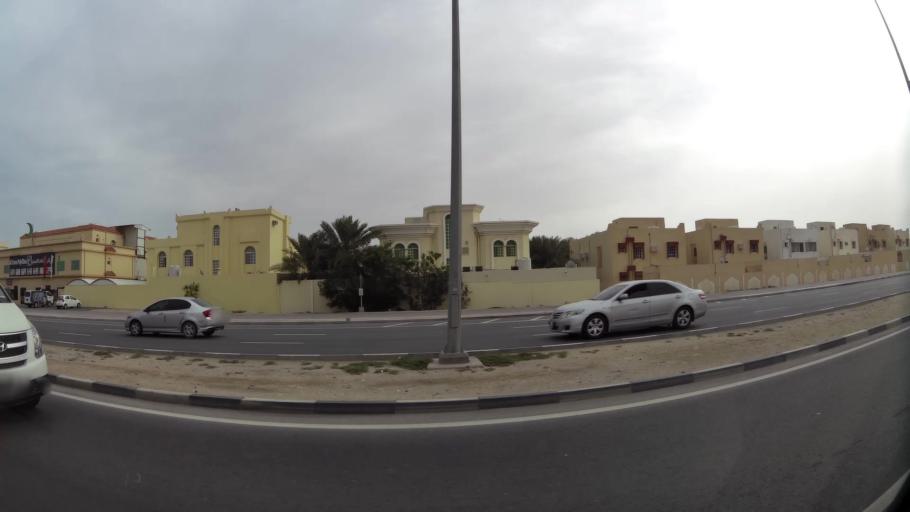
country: QA
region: Baladiyat ad Dawhah
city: Doha
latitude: 25.3352
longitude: 51.4877
